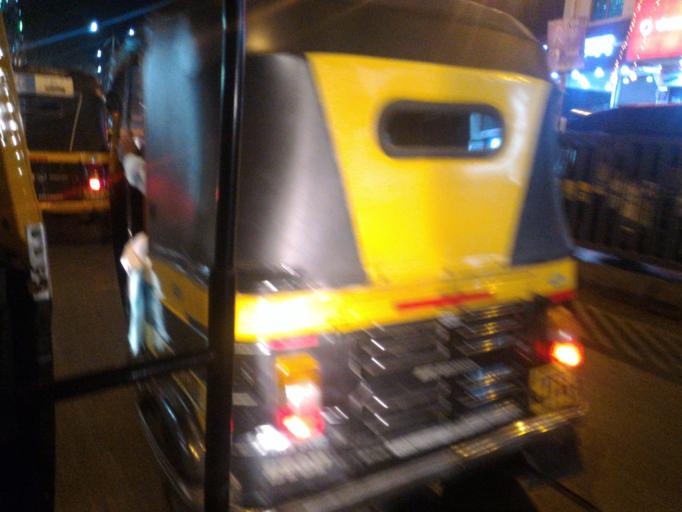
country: IN
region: Maharashtra
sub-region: Thane
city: Thane
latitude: 19.1951
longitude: 72.9770
